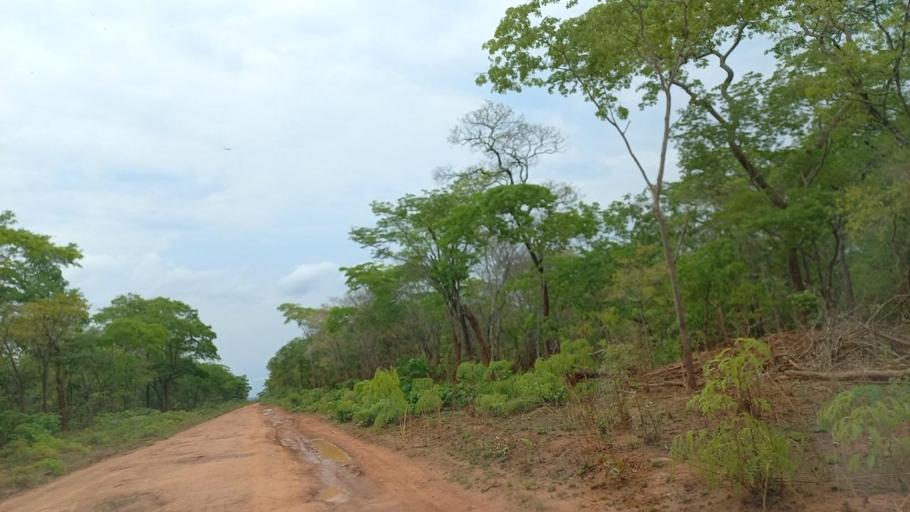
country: ZM
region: North-Western
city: Kalengwa
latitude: -13.6134
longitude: 24.9757
